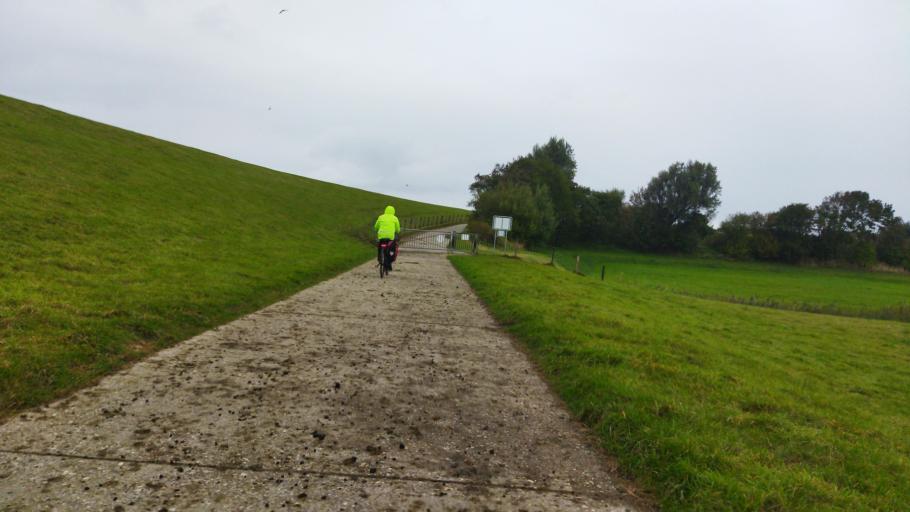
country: DE
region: Lower Saxony
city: Hinte
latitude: 53.4824
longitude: 7.0292
